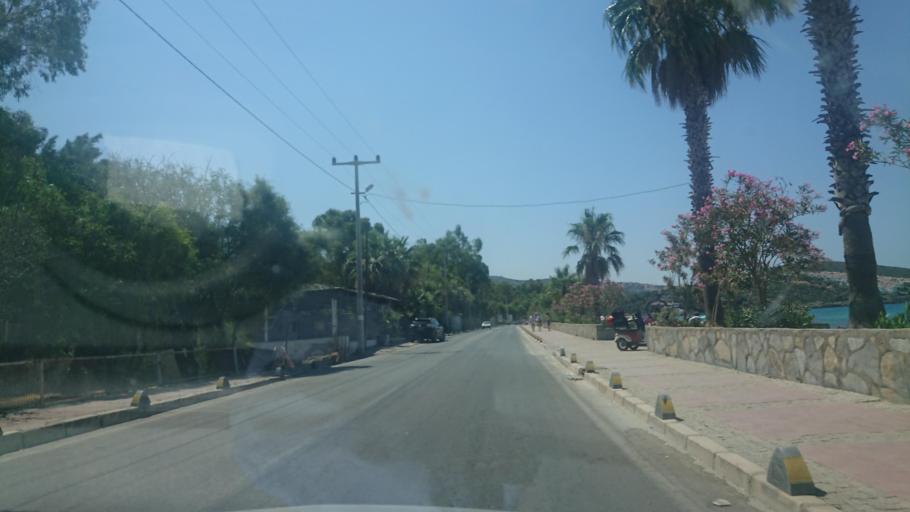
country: TR
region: Aydin
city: Kusadasi
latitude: 37.9036
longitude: 27.2724
